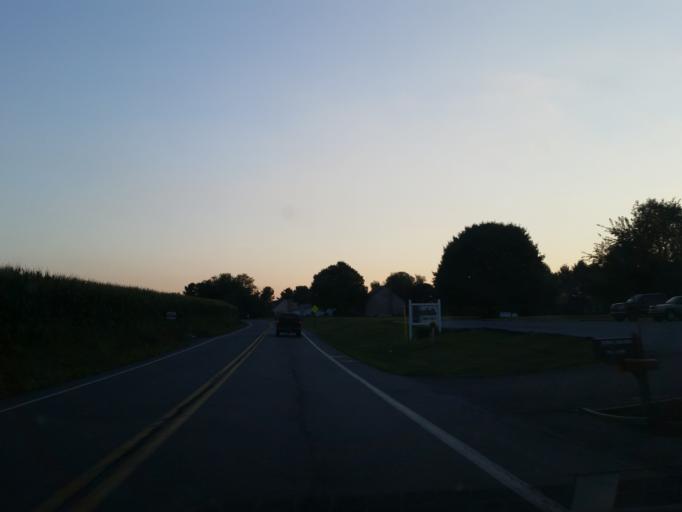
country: US
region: Pennsylvania
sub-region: Lebanon County
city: Cornwall
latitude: 40.2846
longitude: -76.4009
